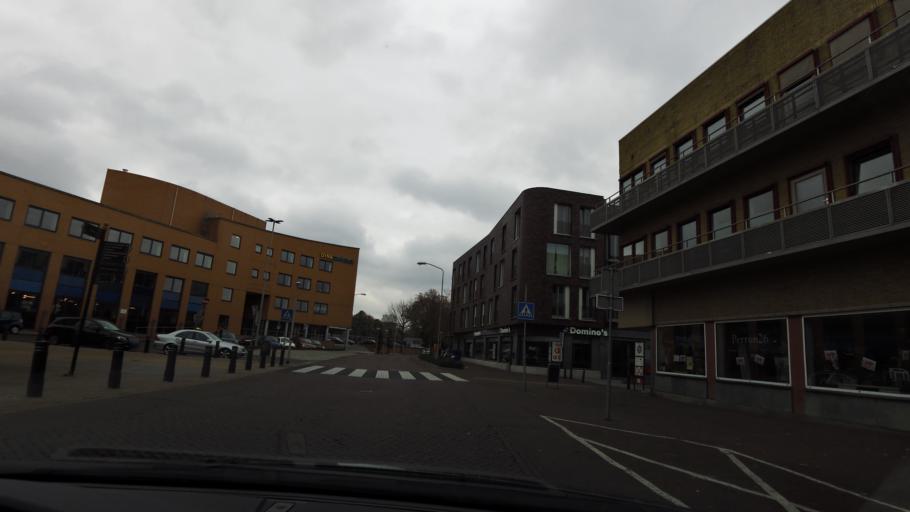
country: NL
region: Limburg
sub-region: Gemeente Sittard-Geleen
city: Sittard
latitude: 51.0015
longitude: 5.8597
